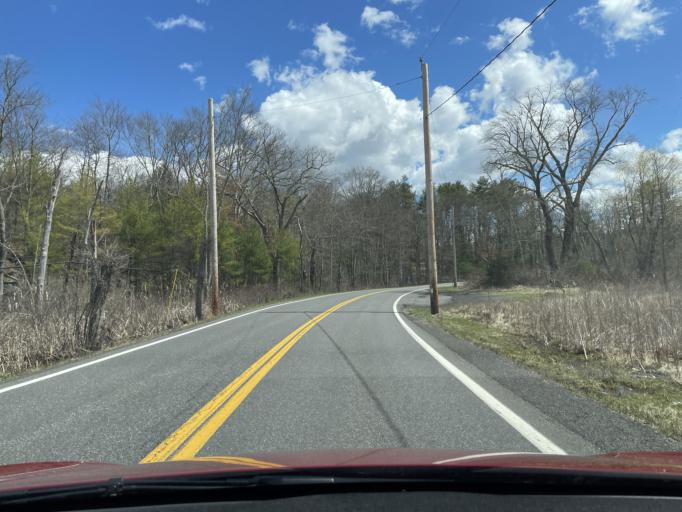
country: US
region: New York
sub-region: Ulster County
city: West Hurley
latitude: 41.9749
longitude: -74.0855
